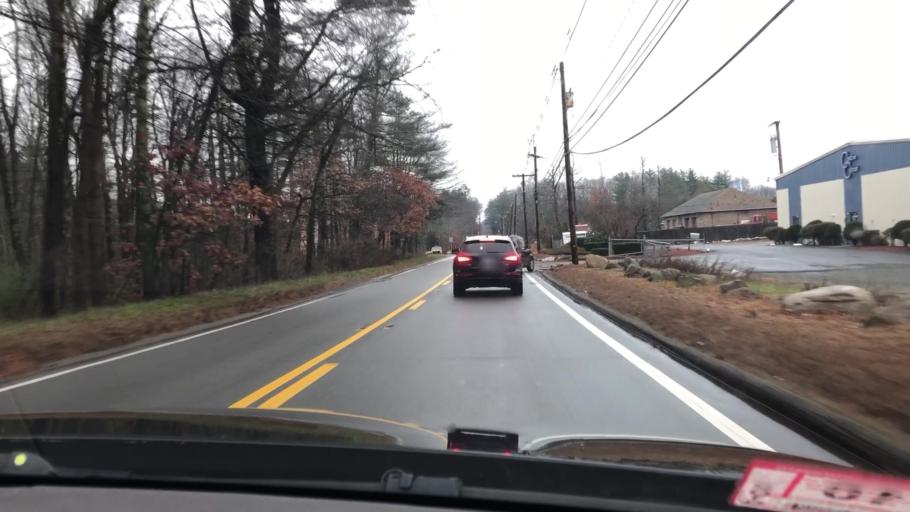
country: US
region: Massachusetts
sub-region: Norfolk County
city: Walpole
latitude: 42.1159
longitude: -71.2810
